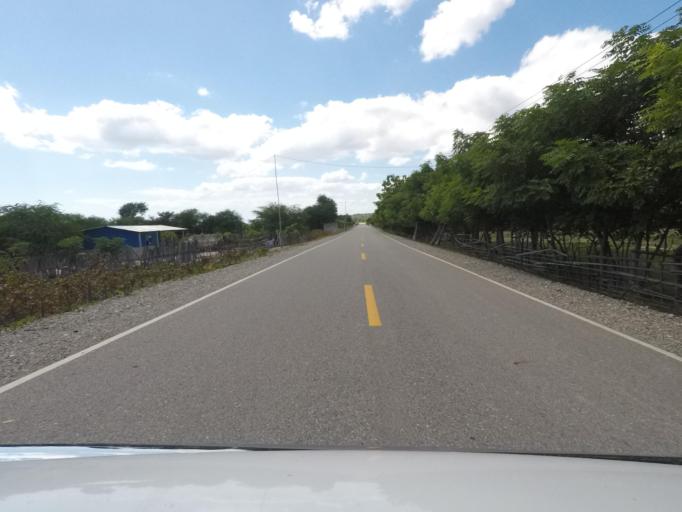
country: TL
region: Baucau
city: Baucau
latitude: -8.4304
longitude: 126.6827
